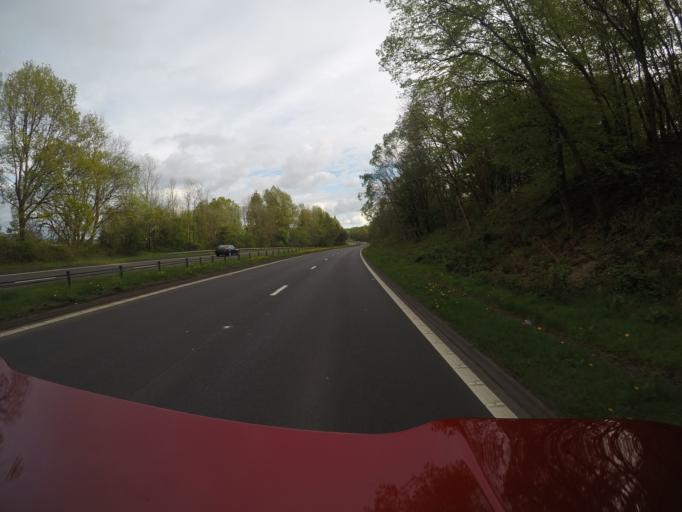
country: GB
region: Scotland
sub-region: West Dunbartonshire
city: Renton
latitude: 55.9826
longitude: -4.5871
